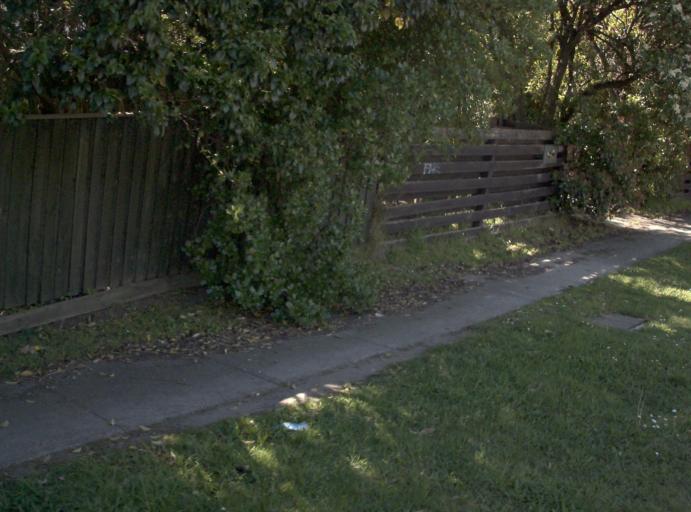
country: AU
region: Victoria
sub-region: Knox
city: Bayswater
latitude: -37.8636
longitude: 145.2654
